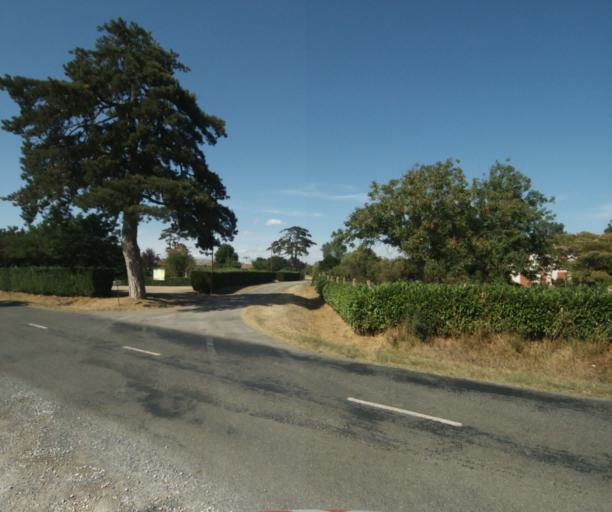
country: FR
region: Midi-Pyrenees
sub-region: Departement de la Haute-Garonne
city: Revel
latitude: 43.4891
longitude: 1.9808
